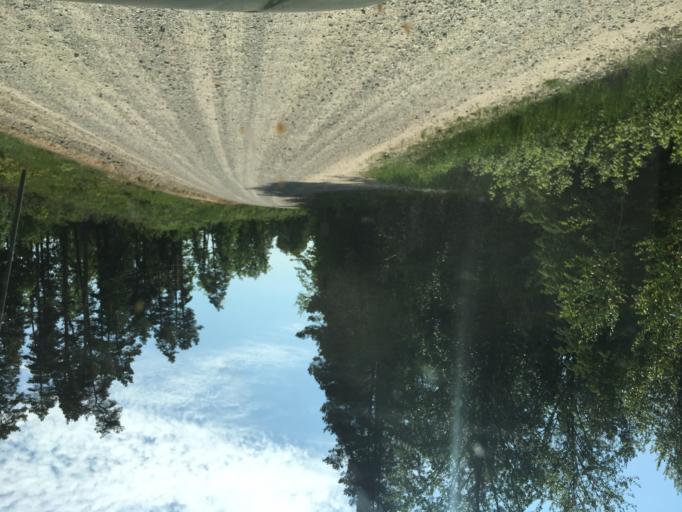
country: LV
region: Talsu Rajons
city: Valdemarpils
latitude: 57.3682
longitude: 22.6213
